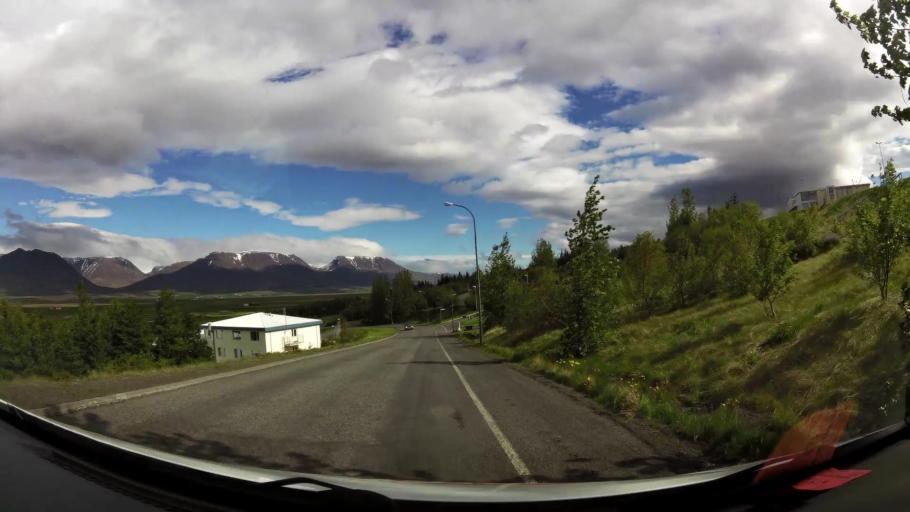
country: IS
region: Northwest
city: Saudarkrokur
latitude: 65.5532
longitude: -19.4492
